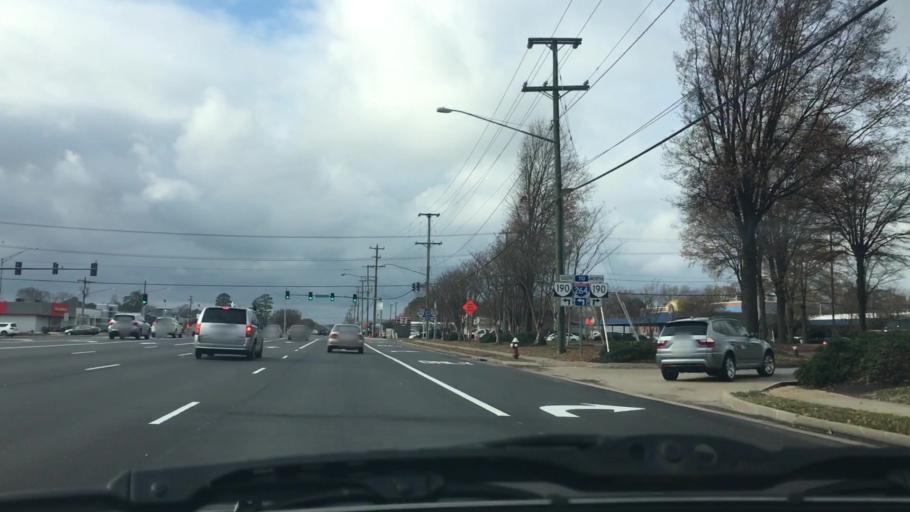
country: US
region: Virginia
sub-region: City of Chesapeake
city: Chesapeake
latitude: 36.8454
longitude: -76.1553
